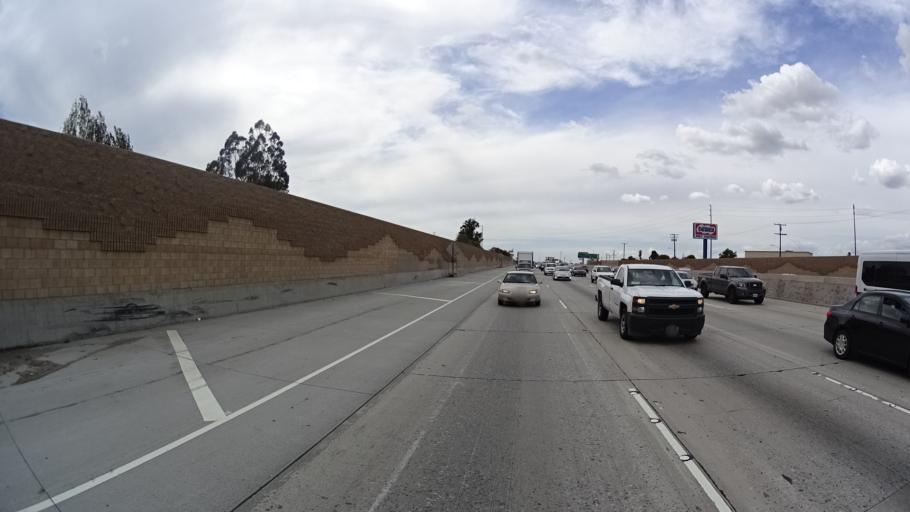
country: US
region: California
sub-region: Los Angeles County
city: Baldwin Park
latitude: 34.0693
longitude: -117.9670
